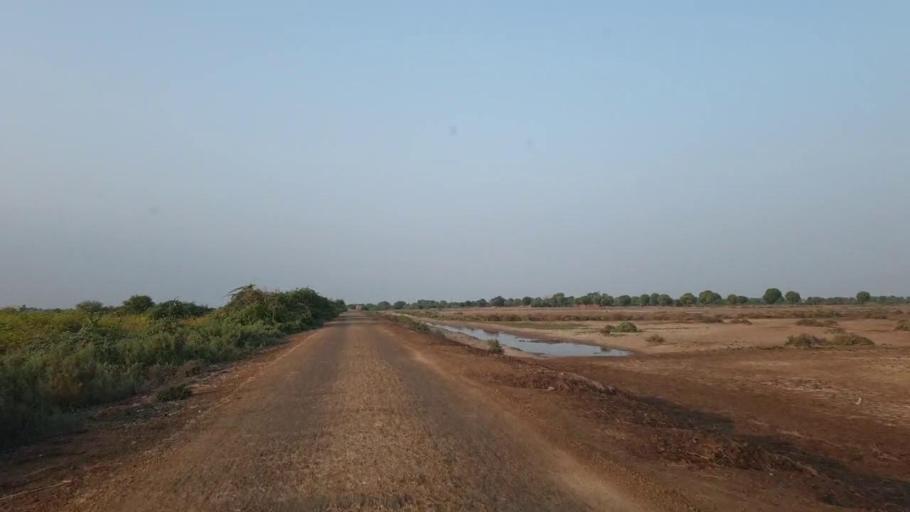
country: PK
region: Sindh
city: Tando Ghulam Ali
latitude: 25.0579
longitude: 68.9604
